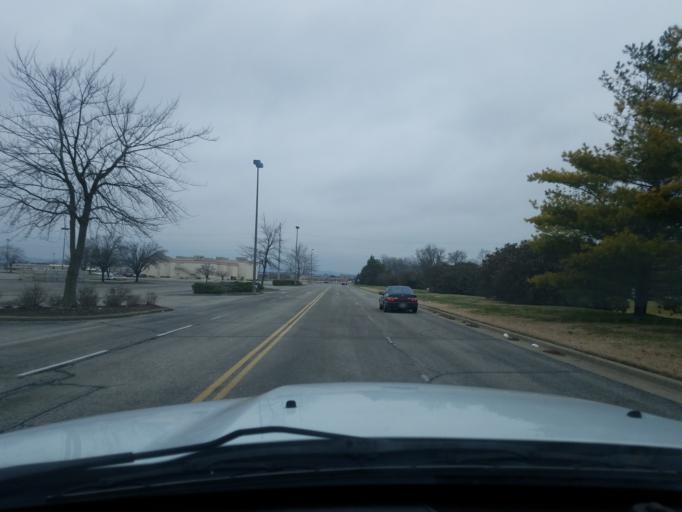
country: US
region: Indiana
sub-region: Clark County
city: Clarksville
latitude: 38.3213
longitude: -85.7590
